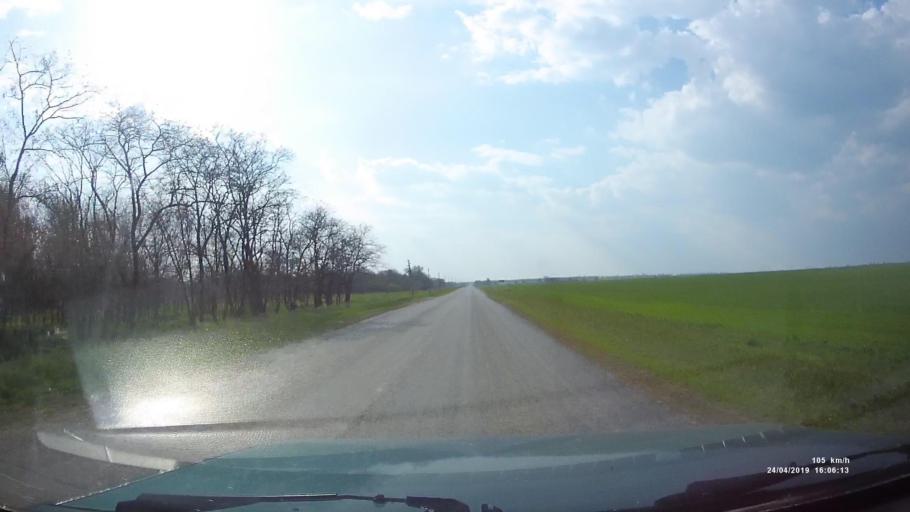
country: RU
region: Rostov
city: Sovetskoye
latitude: 46.6853
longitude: 42.3536
